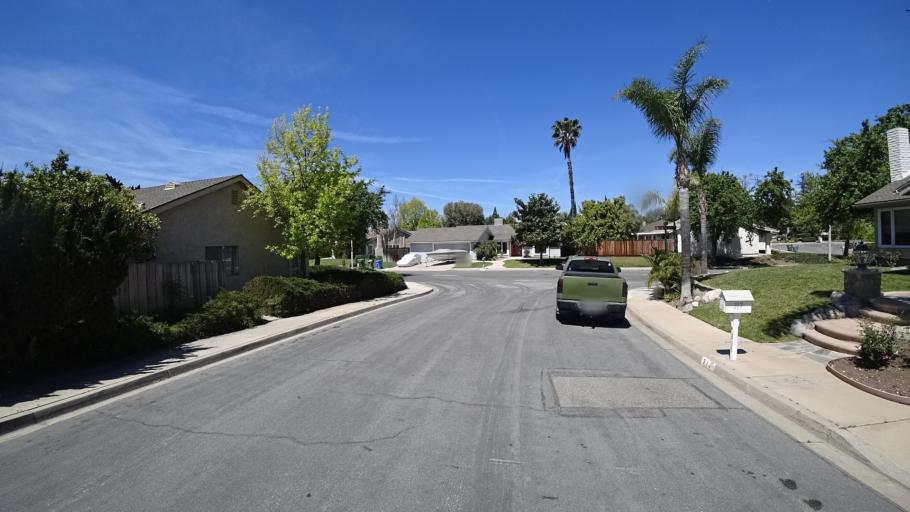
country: US
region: California
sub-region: Ventura County
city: Moorpark
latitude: 34.2241
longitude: -118.8704
